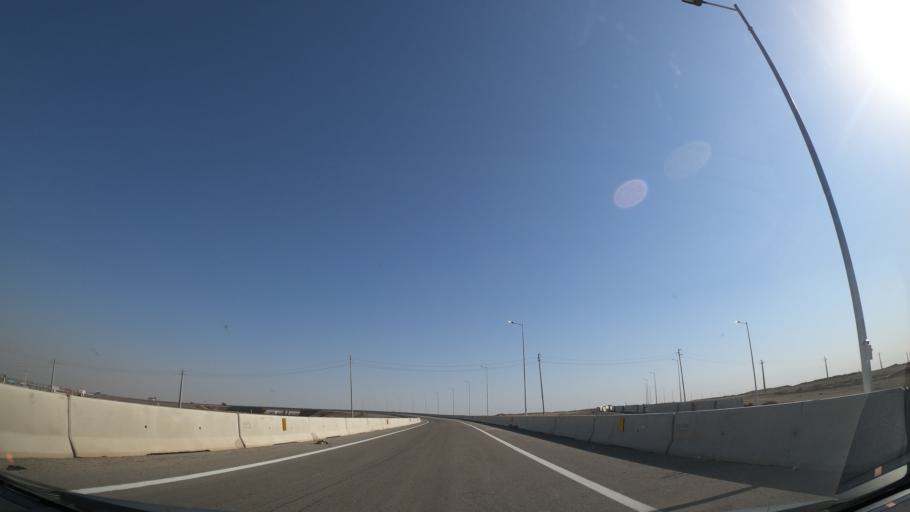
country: IR
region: Tehran
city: Eqbaliyeh
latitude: 35.1355
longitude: 51.5081
